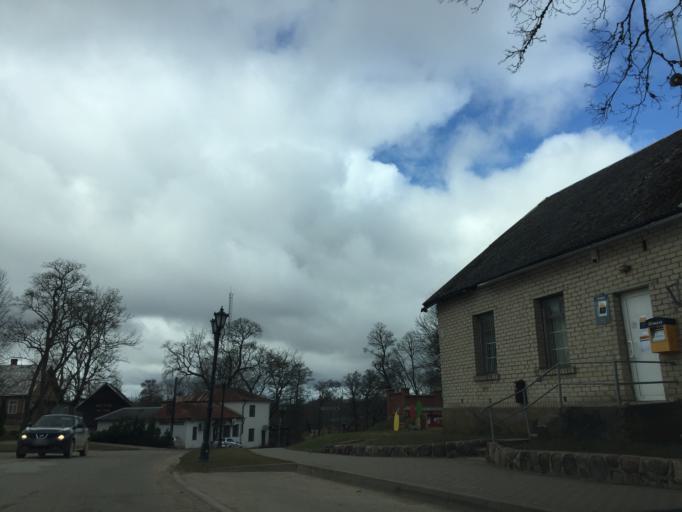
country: LV
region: Ilukste
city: Ilukste
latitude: 56.0667
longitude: 26.1309
